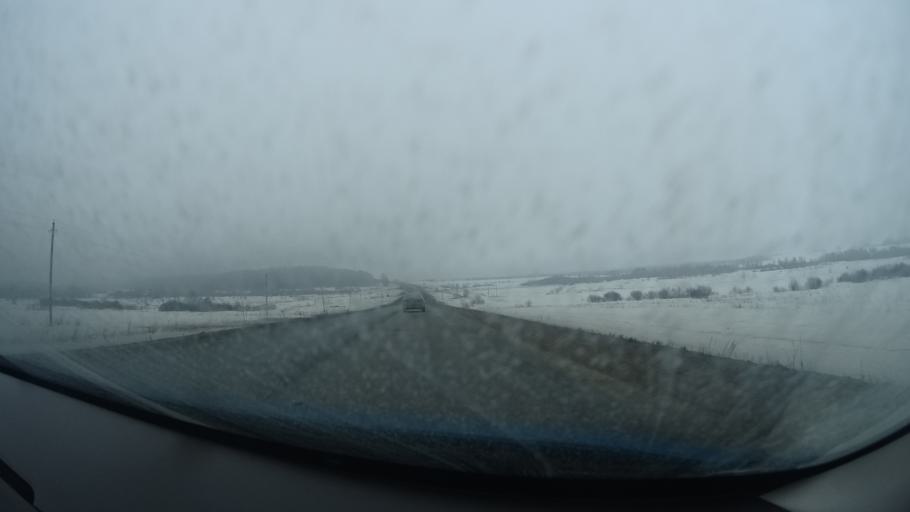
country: RU
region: Perm
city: Kuyeda
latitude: 56.4694
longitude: 55.7166
